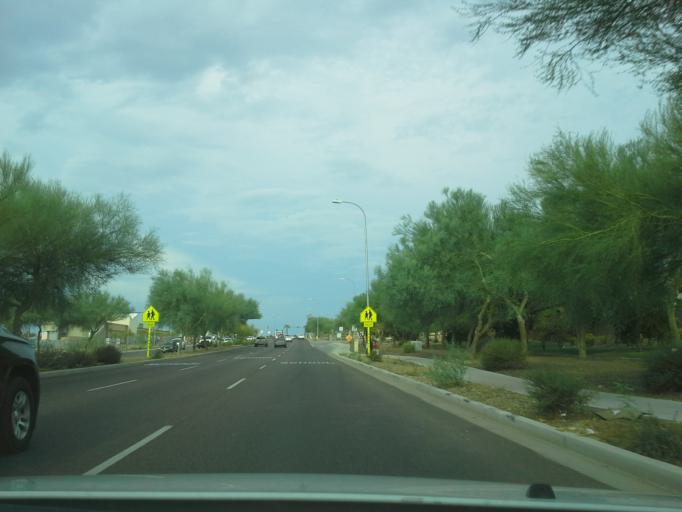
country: US
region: Arizona
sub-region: Maricopa County
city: Guadalupe
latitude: 33.3780
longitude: -111.9995
